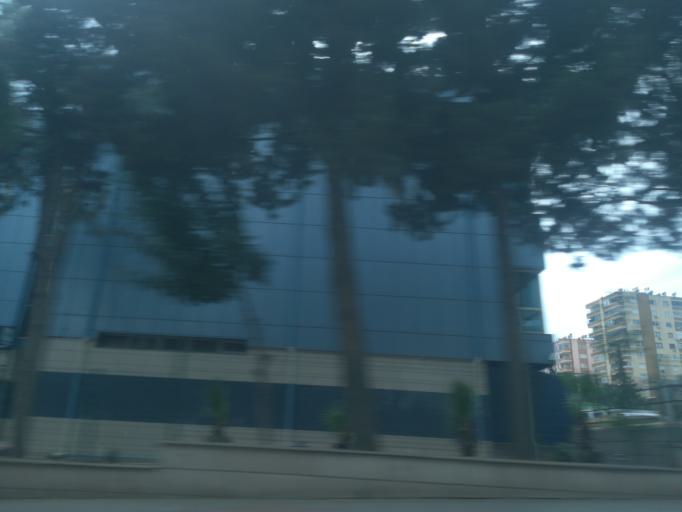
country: TR
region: Adana
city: Adana
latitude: 37.0409
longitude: 35.2922
